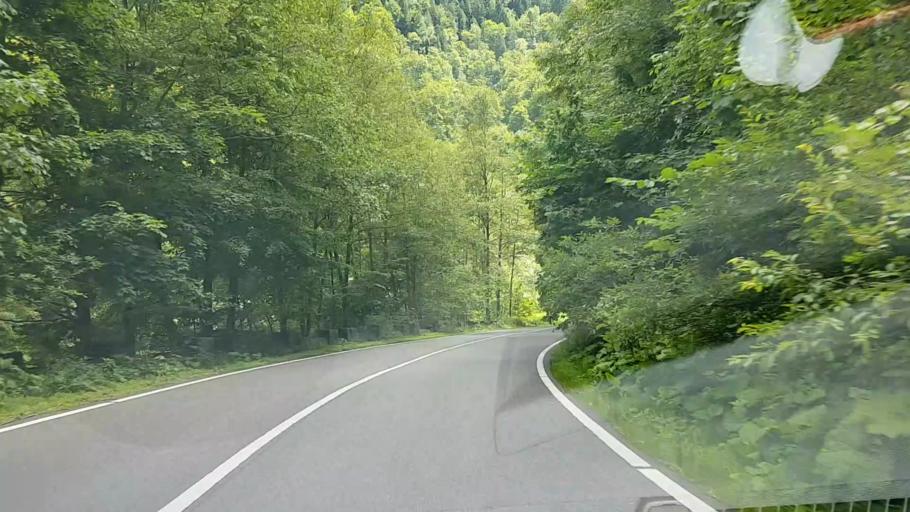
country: RO
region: Suceava
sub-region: Comuna Crucea
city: Crucea
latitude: 47.3121
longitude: 25.6290
